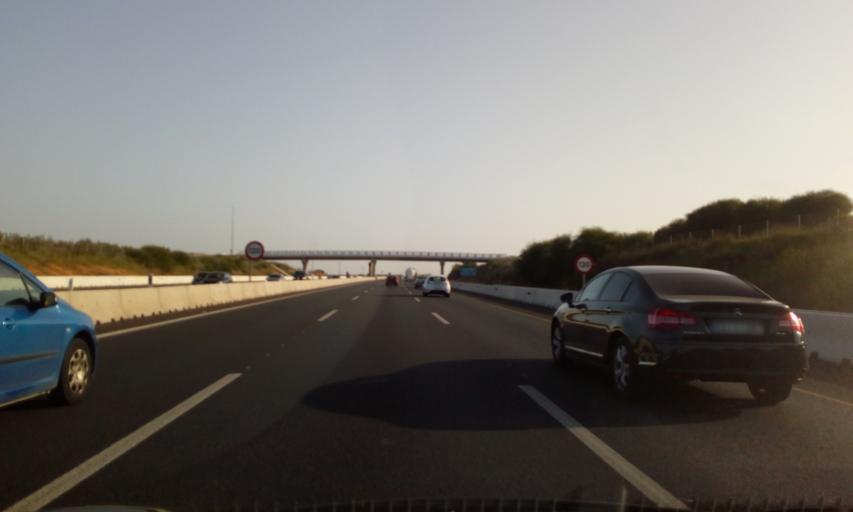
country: ES
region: Andalusia
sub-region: Provincia de Sevilla
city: Bollullos de la Mitacion
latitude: 37.3615
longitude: -6.1353
